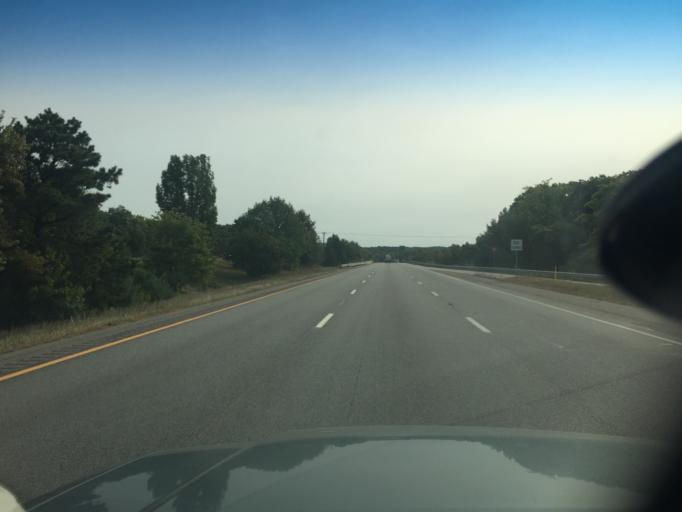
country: US
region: Massachusetts
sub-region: Norfolk County
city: Wrentham
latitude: 42.0372
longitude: -71.3096
